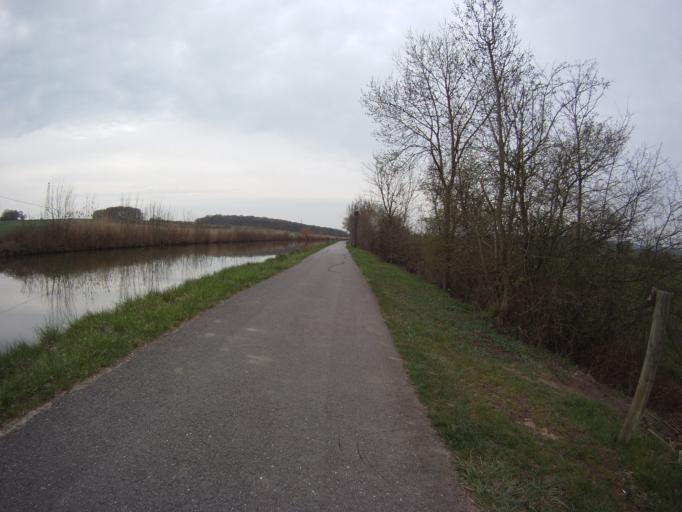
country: FR
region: Lorraine
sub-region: Departement de Meurthe-et-Moselle
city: Laneuveville-devant-Nancy
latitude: 48.6441
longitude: 6.2207
